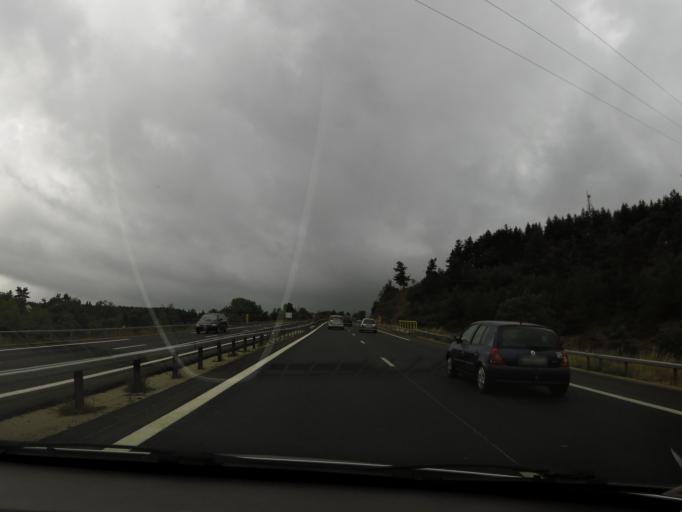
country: FR
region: Languedoc-Roussillon
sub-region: Departement de la Lozere
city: Aumont-Aubrac
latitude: 44.7243
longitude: 3.2803
